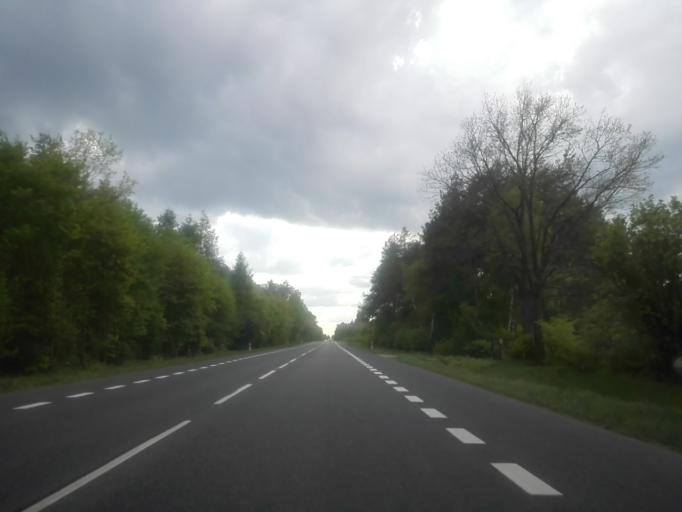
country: PL
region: Masovian Voivodeship
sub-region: Powiat ostrowski
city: Ostrow Mazowiecka
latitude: 52.8390
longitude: 21.9600
